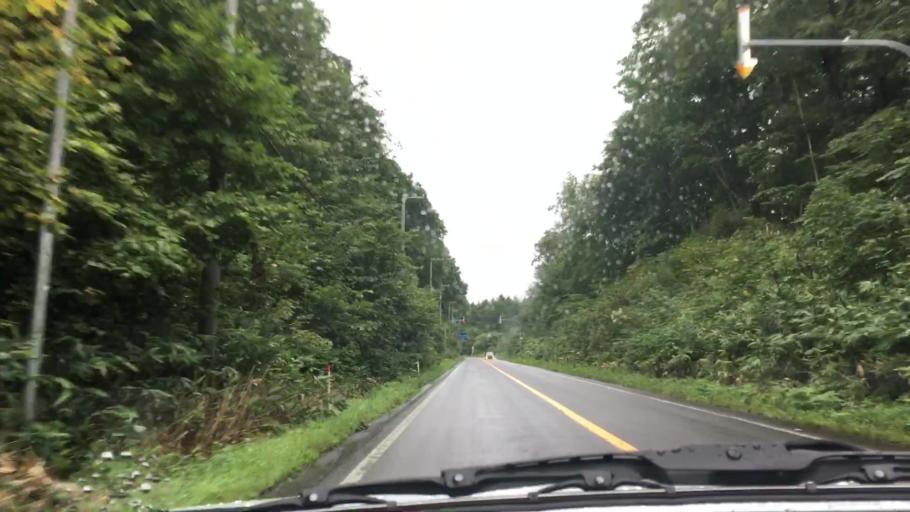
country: JP
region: Hokkaido
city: Niseko Town
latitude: 42.6135
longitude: 140.7291
